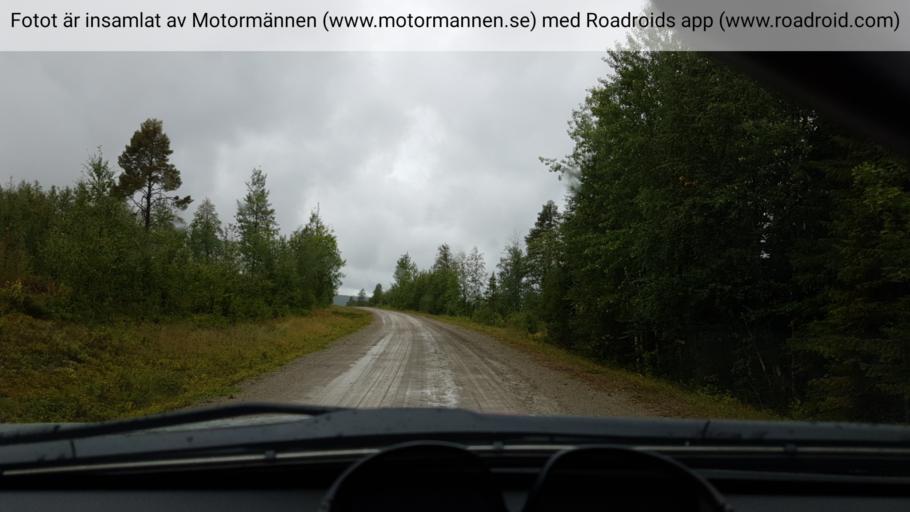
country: SE
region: Vaesterbotten
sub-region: Asele Kommun
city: Insjon
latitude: 64.7880
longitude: 17.6104
